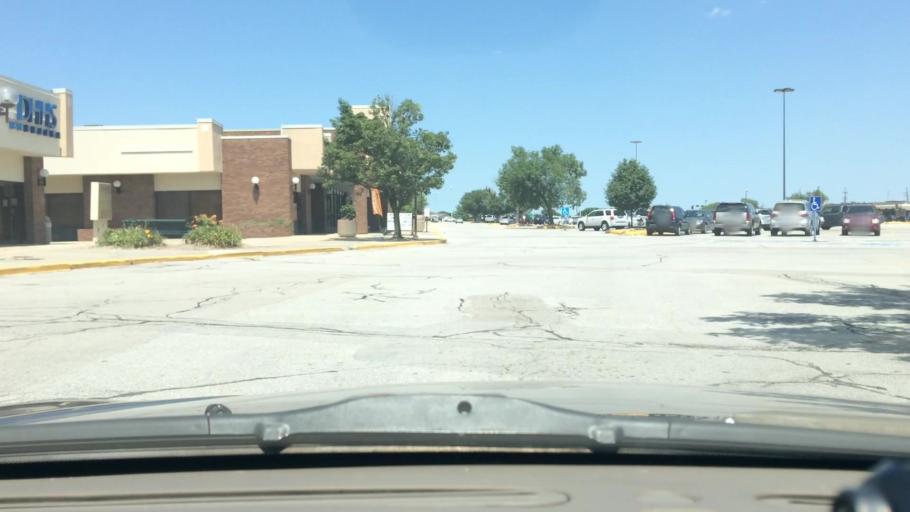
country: US
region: Nebraska
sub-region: Sarpy County
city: La Vista
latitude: 41.1772
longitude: -96.0453
